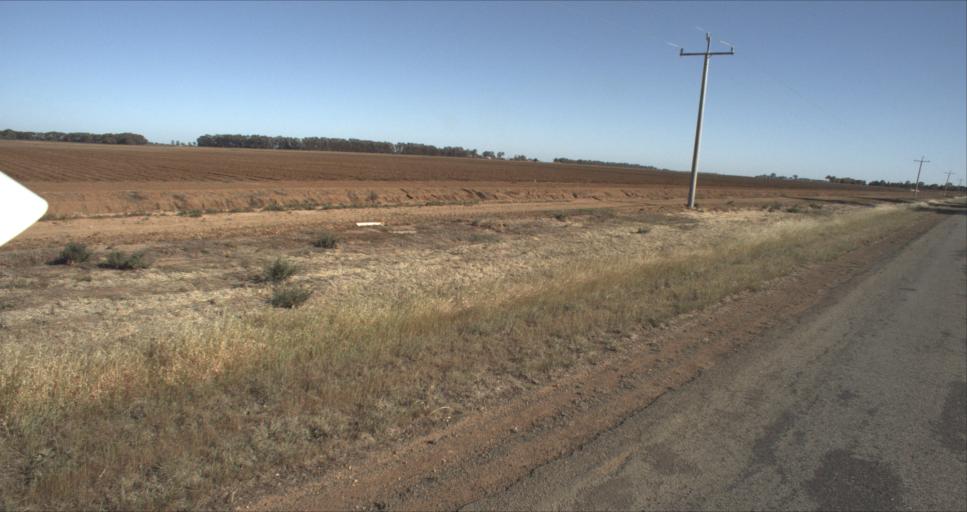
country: AU
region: New South Wales
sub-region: Leeton
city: Leeton
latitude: -34.5994
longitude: 146.2580
